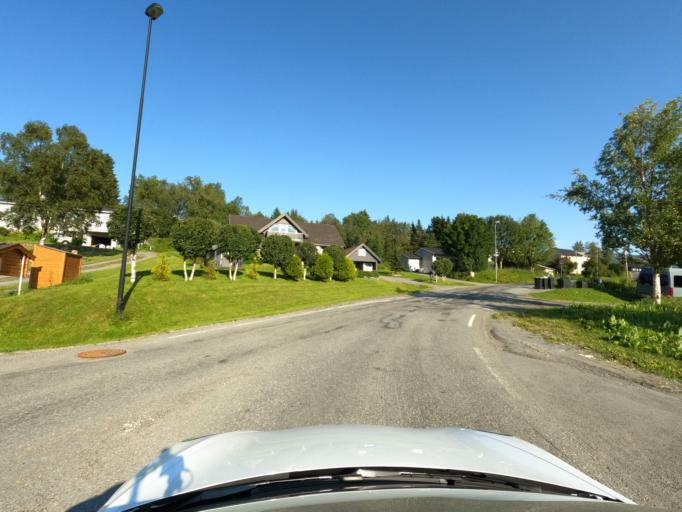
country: NO
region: Nordland
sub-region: Narvik
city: Bjerkvik
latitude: 68.5539
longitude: 17.5587
